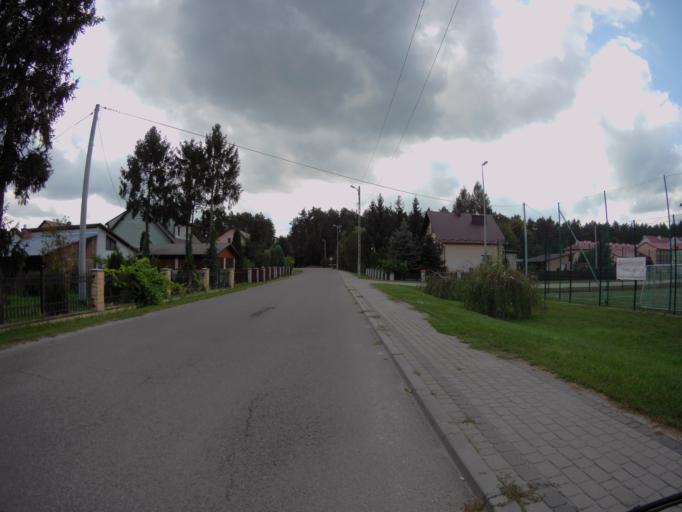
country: PL
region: Subcarpathian Voivodeship
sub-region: Powiat lezajski
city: Brzoza Krolewska
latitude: 50.2441
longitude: 22.3218
